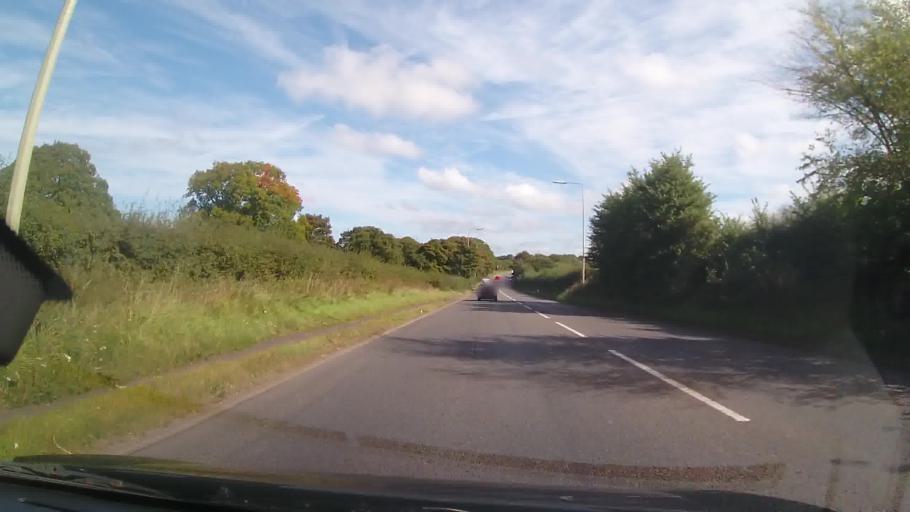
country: GB
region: England
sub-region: Staffordshire
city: Featherstone
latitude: 52.6564
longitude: -2.0718
